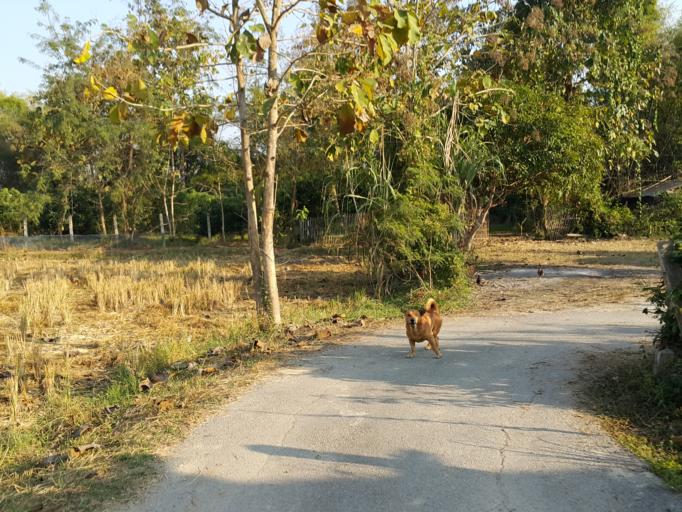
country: TH
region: Chiang Mai
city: San Kamphaeng
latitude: 18.7957
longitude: 99.1090
